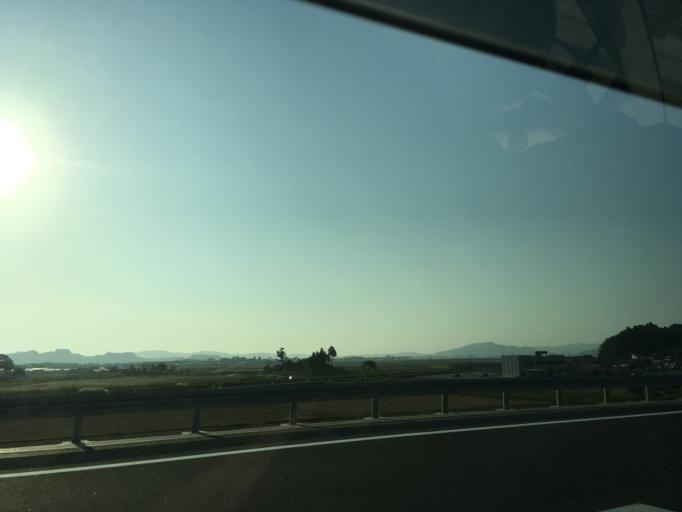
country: JP
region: Miyagi
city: Ishinomaki
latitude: 38.4966
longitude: 141.2877
